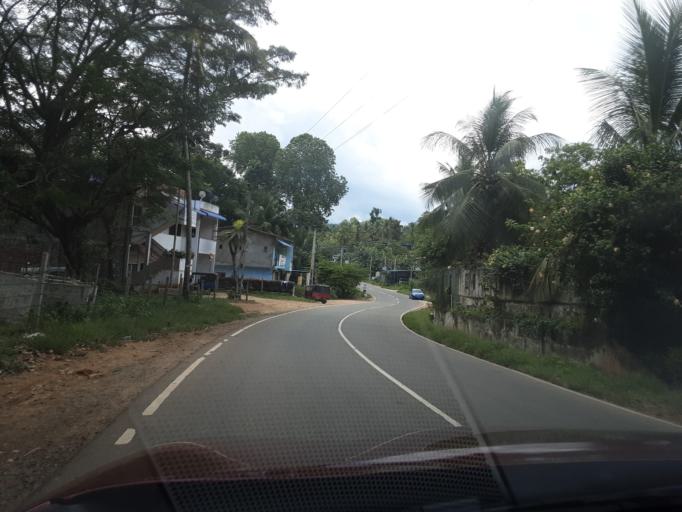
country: LK
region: Uva
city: Monaragala
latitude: 6.8977
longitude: 81.2433
